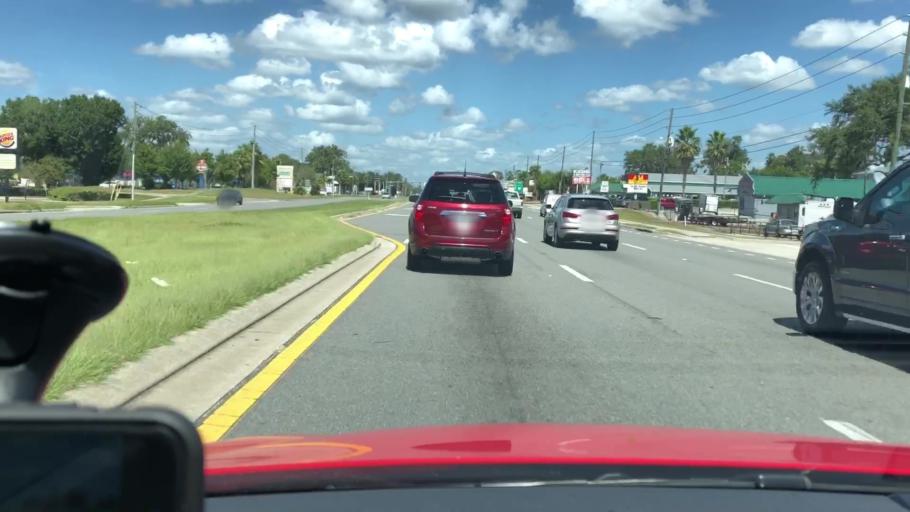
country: US
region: Florida
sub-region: Volusia County
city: De Land Southwest
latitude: 28.9951
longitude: -81.3024
